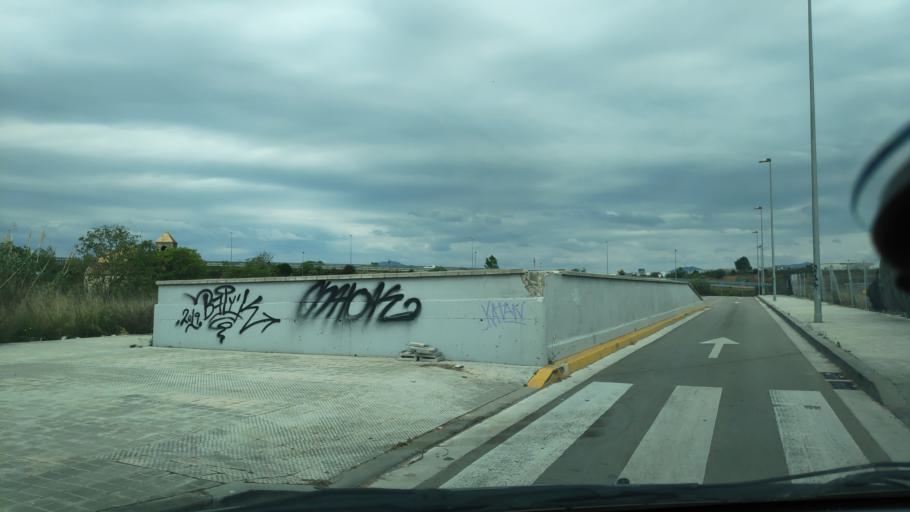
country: ES
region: Catalonia
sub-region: Provincia de Barcelona
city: Barbera del Valles
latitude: 41.5132
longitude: 2.1047
